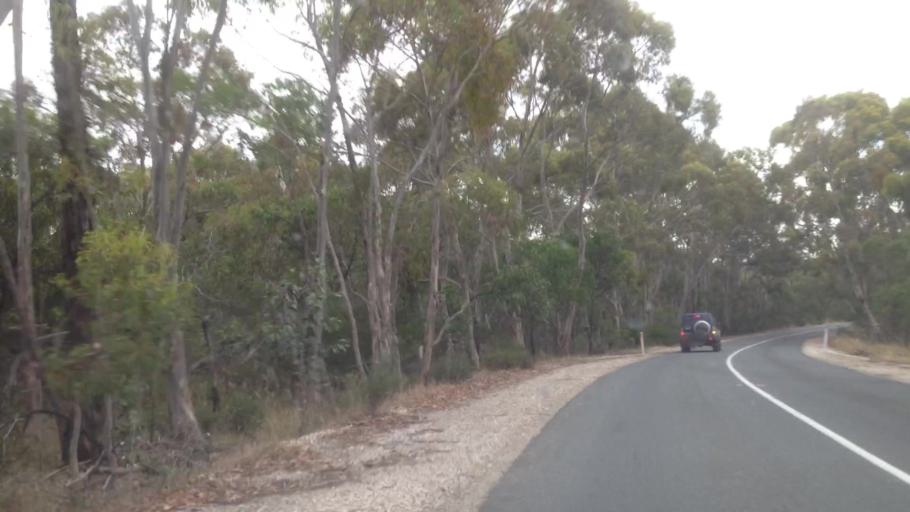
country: AU
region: South Australia
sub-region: Adelaide Hills
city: Birdwood
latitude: -34.7646
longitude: 138.9453
